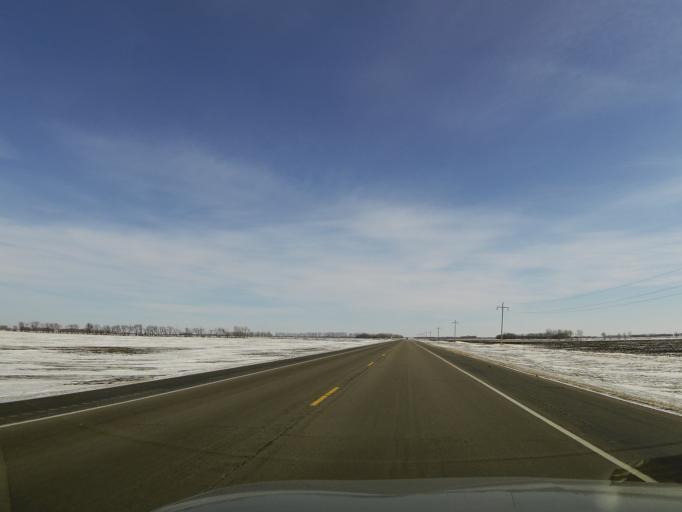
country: US
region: North Dakota
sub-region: Walsh County
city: Grafton
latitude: 48.4121
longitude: -97.2512
